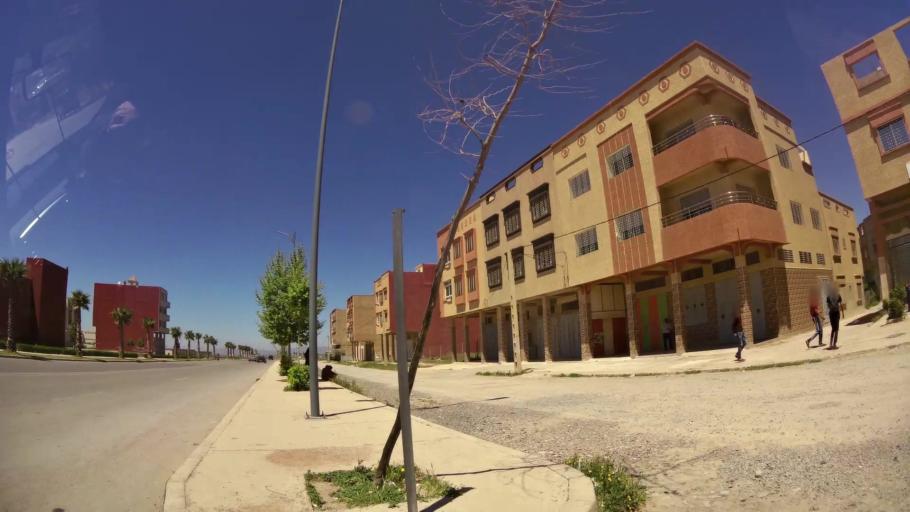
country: MA
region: Oriental
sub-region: Oujda-Angad
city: Oujda
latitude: 34.6759
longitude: -1.8594
